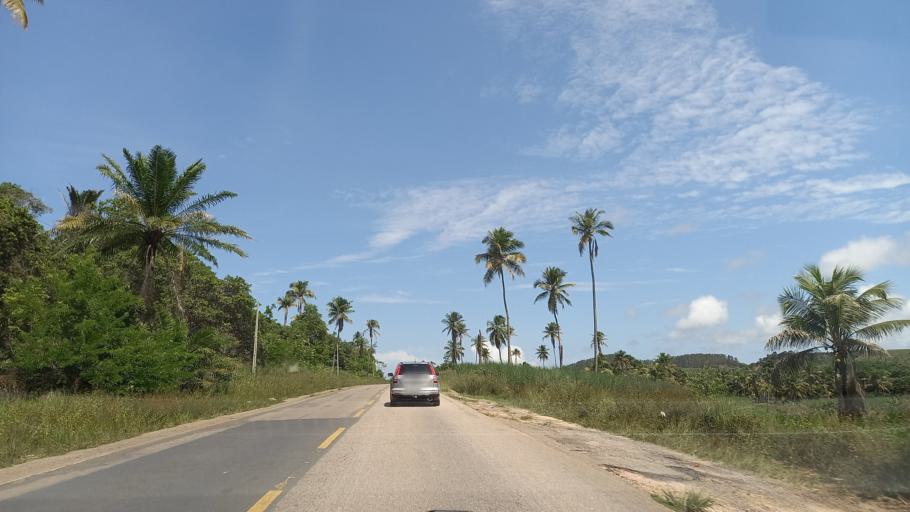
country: BR
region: Pernambuco
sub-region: Sao Jose Da Coroa Grande
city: Sao Jose da Coroa Grande
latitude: -8.8678
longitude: -35.1645
